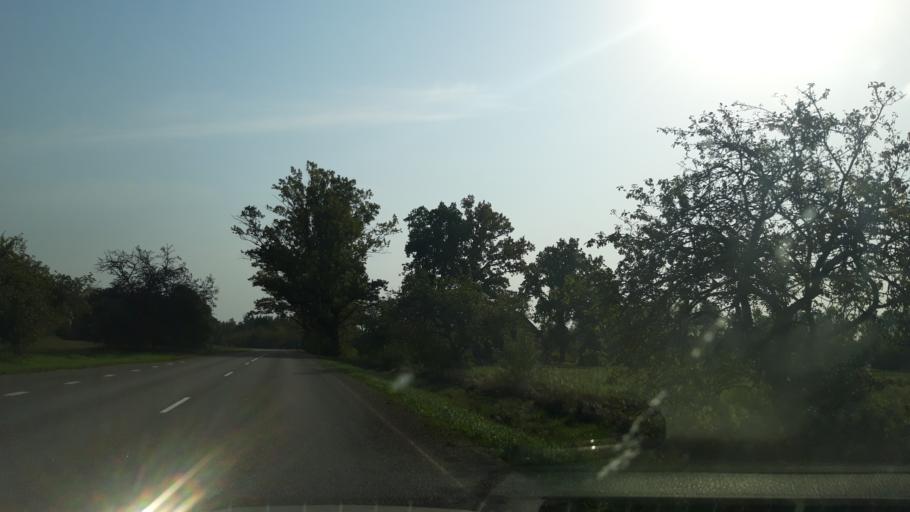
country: LV
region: Koceni
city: Koceni
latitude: 57.6258
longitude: 25.2691
